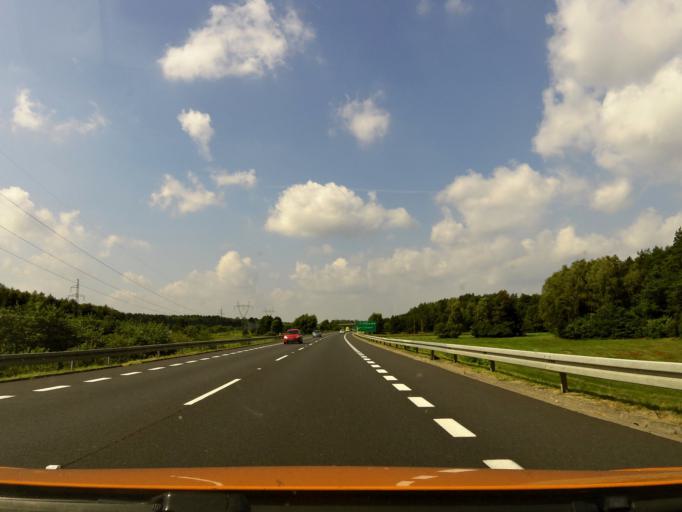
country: PL
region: West Pomeranian Voivodeship
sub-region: Powiat goleniowski
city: Goleniow
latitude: 53.5881
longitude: 14.8362
